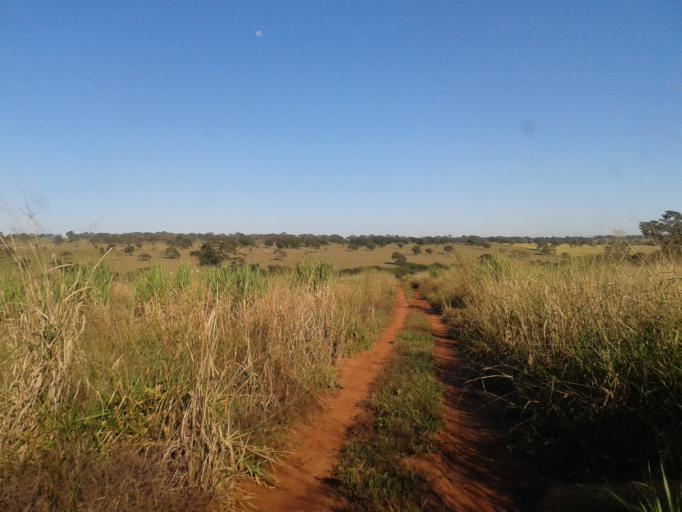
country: BR
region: Minas Gerais
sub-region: Santa Vitoria
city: Santa Vitoria
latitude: -19.0199
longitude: -50.3769
